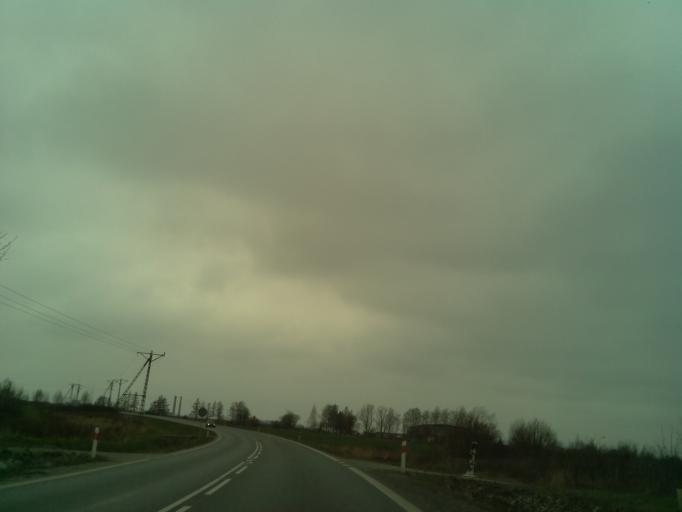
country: PL
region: Lower Silesian Voivodeship
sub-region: Powiat sredzki
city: Udanin
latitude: 50.9970
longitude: 16.4575
